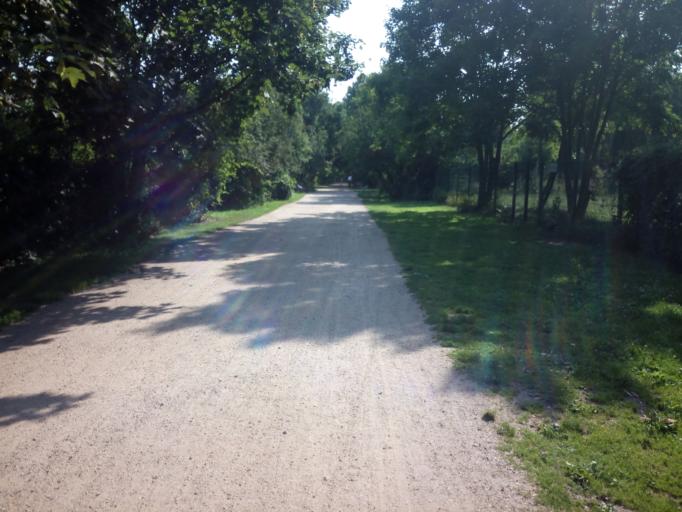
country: DE
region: Berlin
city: Tempelhof Bezirk
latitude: 52.4710
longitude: 13.4216
